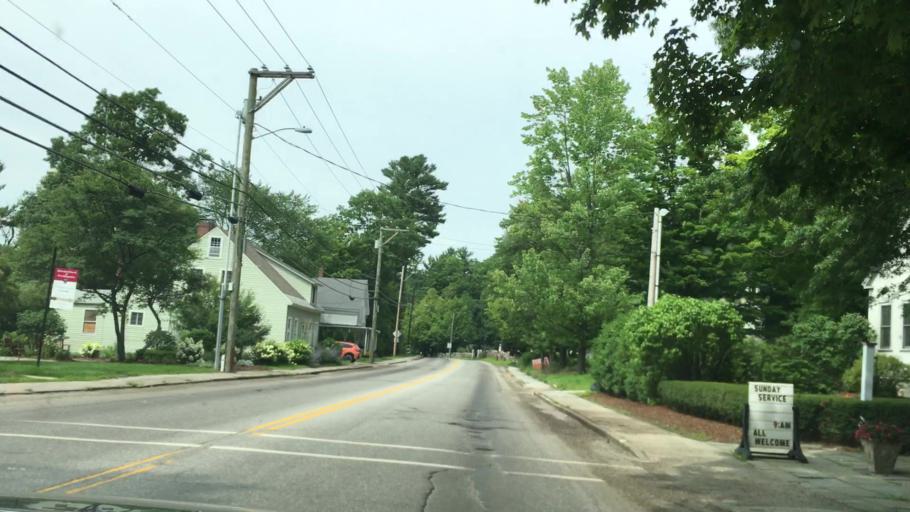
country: US
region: New Hampshire
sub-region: Hillsborough County
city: Peterborough
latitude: 42.8806
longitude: -71.9467
